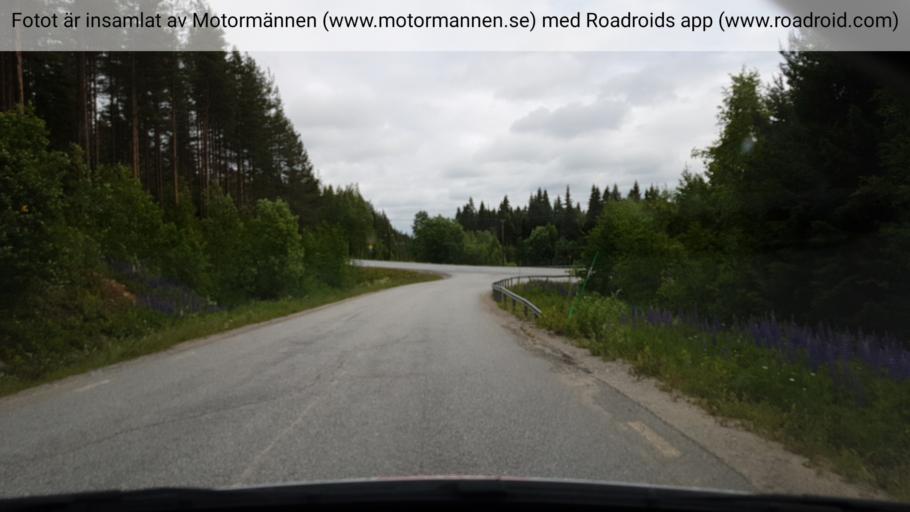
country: SE
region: Vaesterbotten
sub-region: Bjurholms Kommun
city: Bjurholm
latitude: 63.9331
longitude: 19.3538
